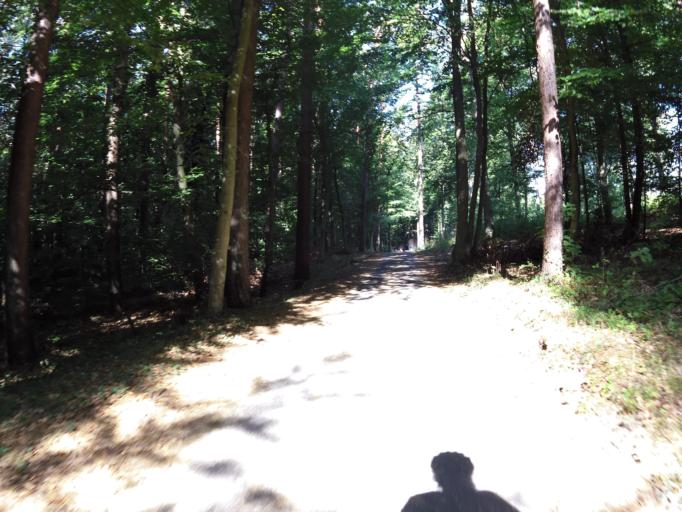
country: DE
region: Mecklenburg-Vorpommern
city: Loddin
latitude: 54.0284
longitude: 14.0469
